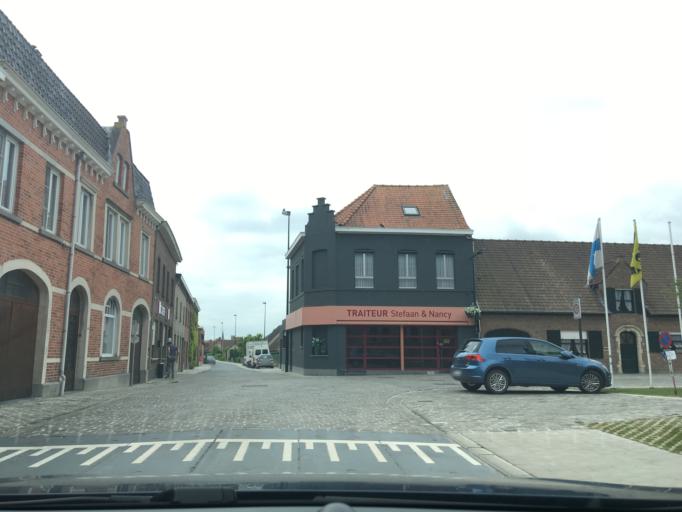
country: BE
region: Flanders
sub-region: Provincie West-Vlaanderen
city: Ledegem
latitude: 50.8672
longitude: 3.0888
